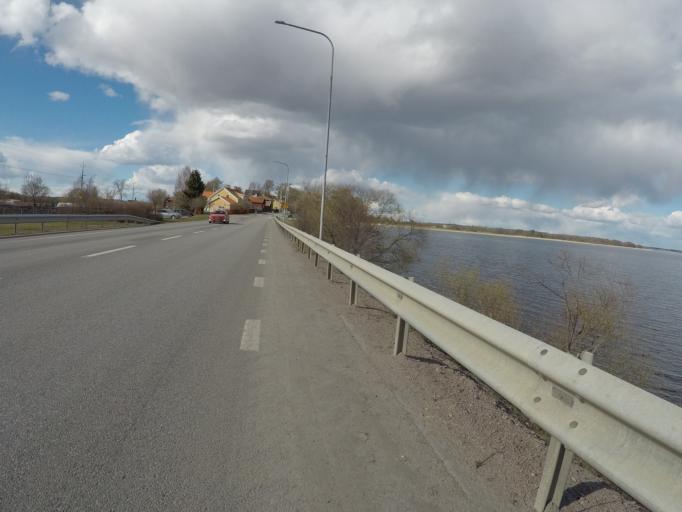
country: SE
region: Vaestmanland
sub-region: Hallstahammars Kommun
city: Kolback
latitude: 59.5071
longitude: 16.2632
